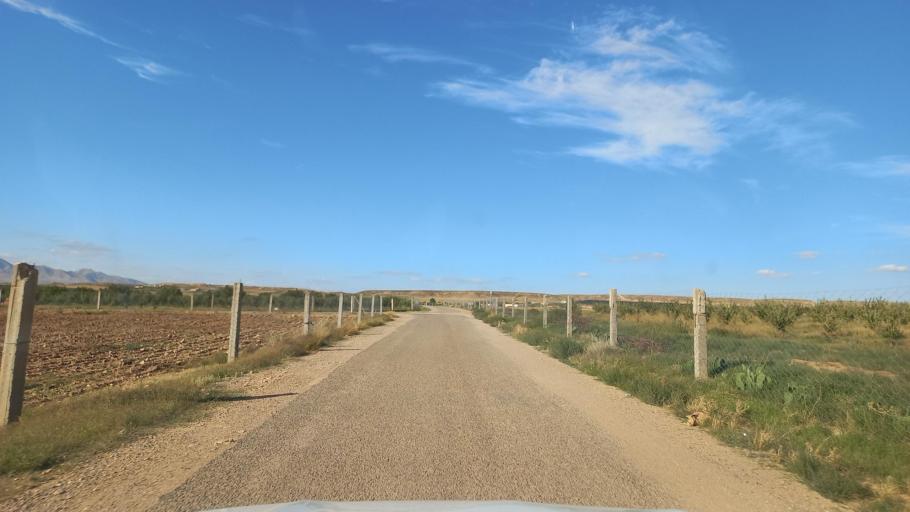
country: TN
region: Al Qasrayn
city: Sbiba
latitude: 35.3364
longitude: 9.1188
